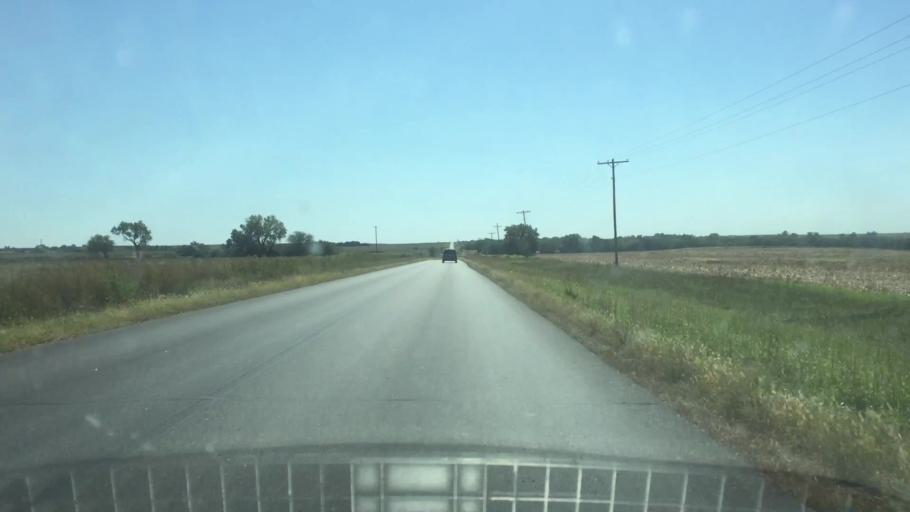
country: US
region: Kansas
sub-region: Marshall County
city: Marysville
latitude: 39.8884
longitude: -96.6011
